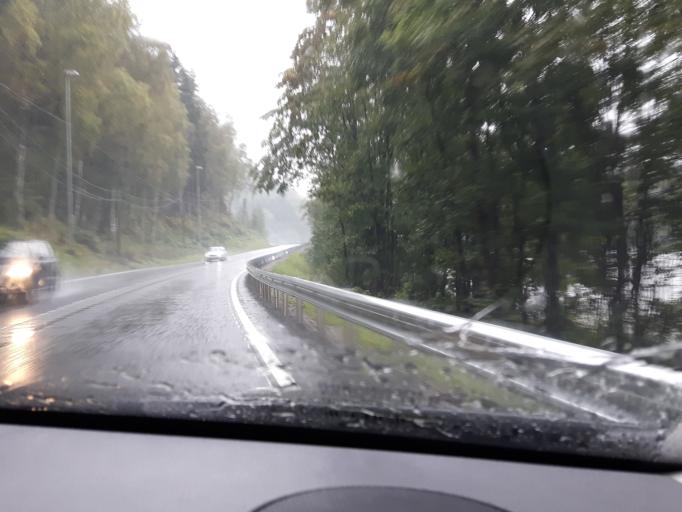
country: NO
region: Vest-Agder
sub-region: Lindesnes
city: Vigeland
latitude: 58.0546
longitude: 7.3717
